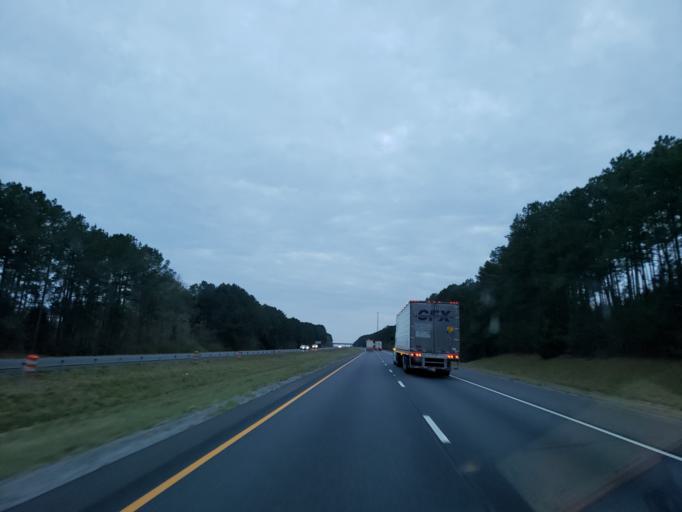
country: US
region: Alabama
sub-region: Sumter County
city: York
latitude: 32.5164
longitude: -88.3104
